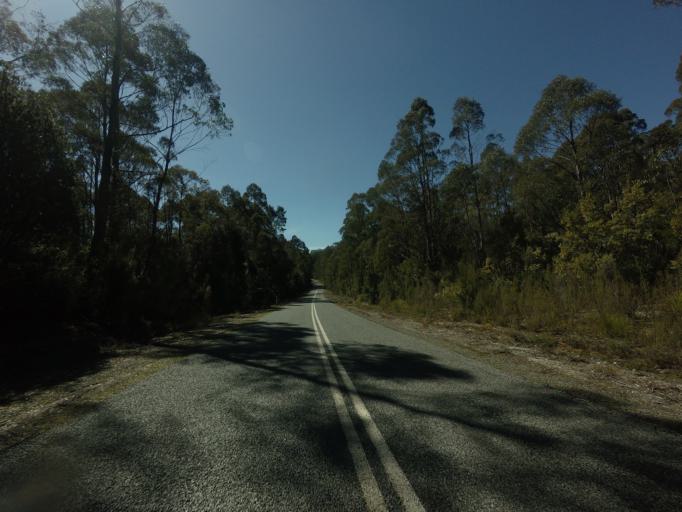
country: AU
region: Tasmania
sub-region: Huon Valley
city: Geeveston
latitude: -42.7662
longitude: 146.3971
